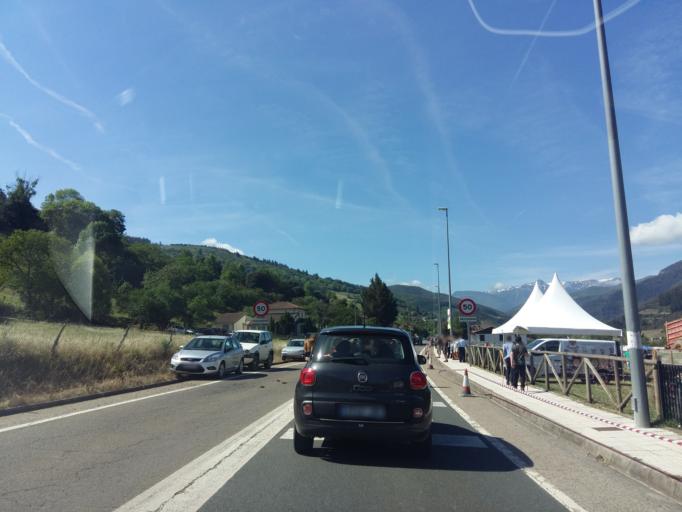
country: ES
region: Cantabria
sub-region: Provincia de Cantabria
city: Potes
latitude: 43.1745
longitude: -4.6005
